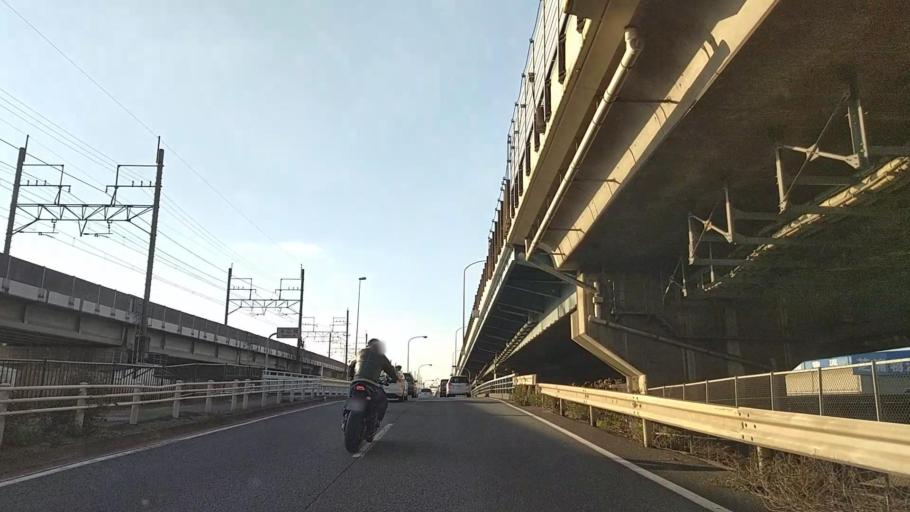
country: JP
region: Chiba
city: Funabashi
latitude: 35.6899
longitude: 139.9708
